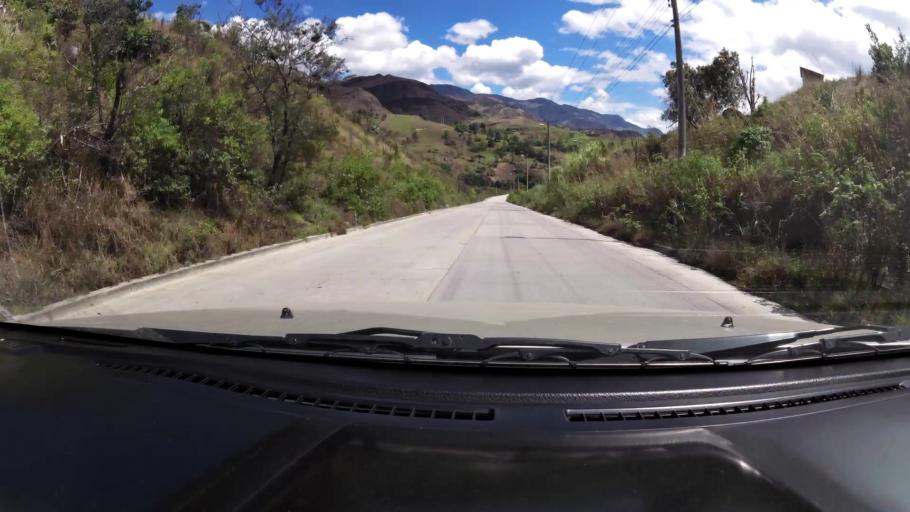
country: EC
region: Azuay
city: Cuenca
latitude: -3.1884
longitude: -79.1716
